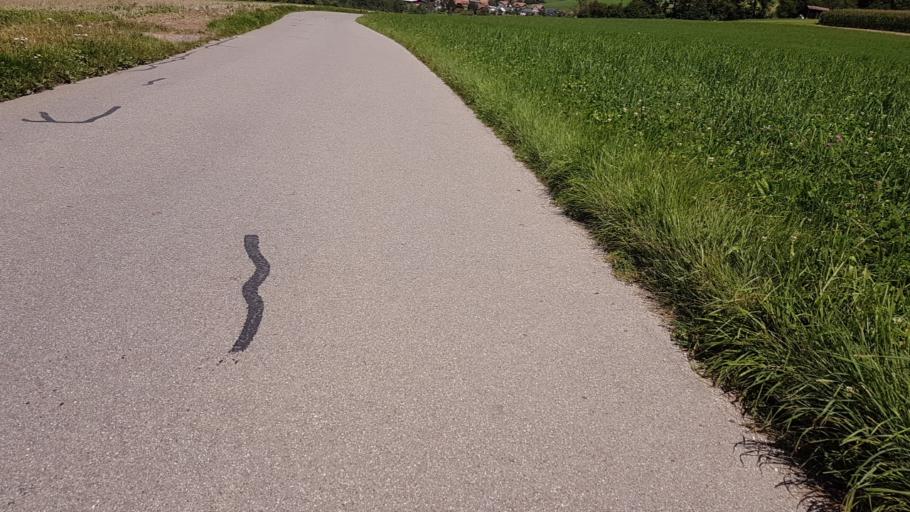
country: CH
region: Lucerne
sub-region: Entlebuch District
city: Oberdiessbach
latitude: 46.8587
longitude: 7.6253
